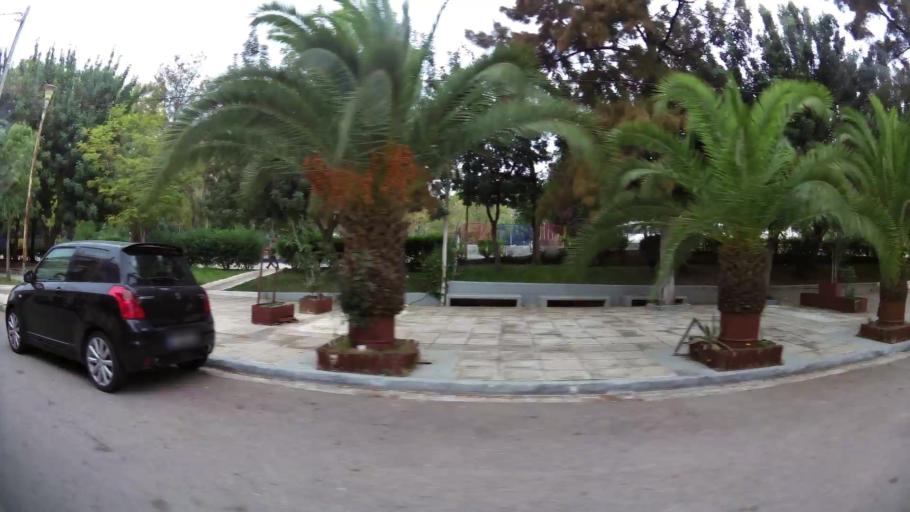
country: GR
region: Attica
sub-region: Nomarchia Athinas
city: Chaidari
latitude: 38.0006
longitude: 23.6774
